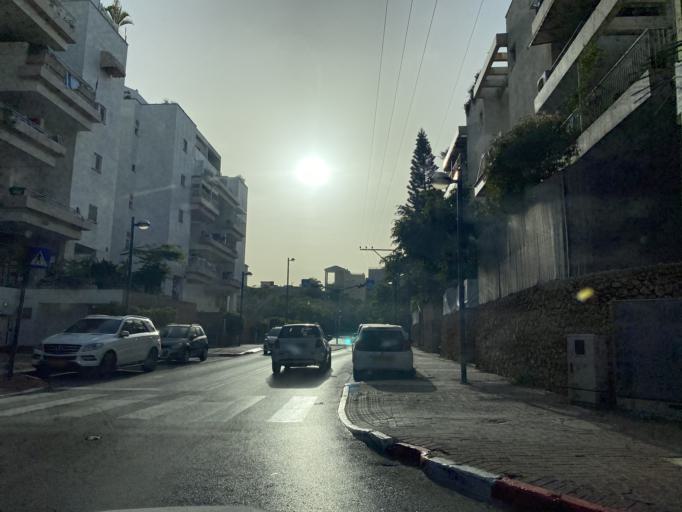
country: IL
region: Central District
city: Kfar Saba
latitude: 32.1787
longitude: 34.9067
